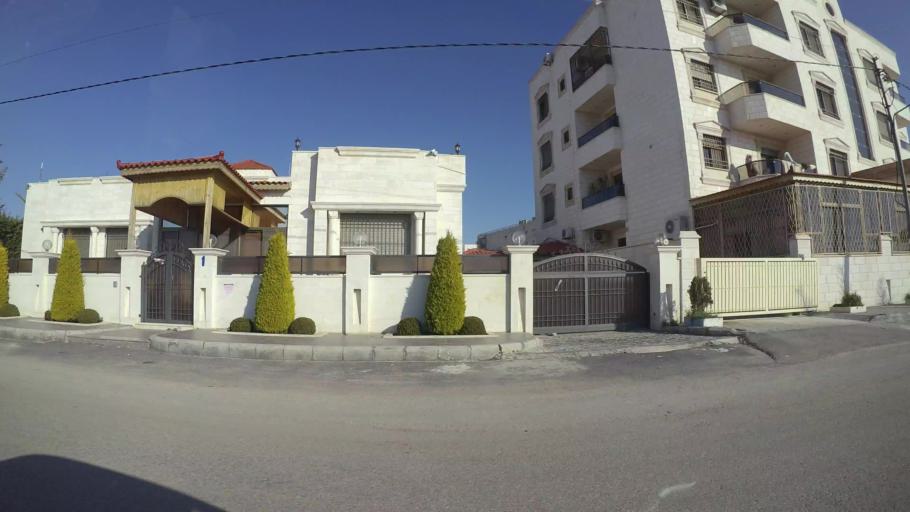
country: JO
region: Amman
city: Al Quwaysimah
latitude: 31.9016
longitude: 35.9260
